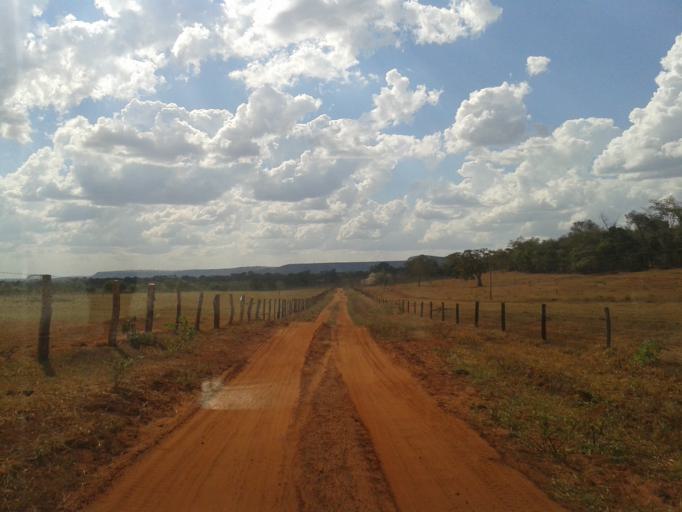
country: BR
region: Minas Gerais
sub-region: Santa Vitoria
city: Santa Vitoria
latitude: -19.2031
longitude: -49.9701
